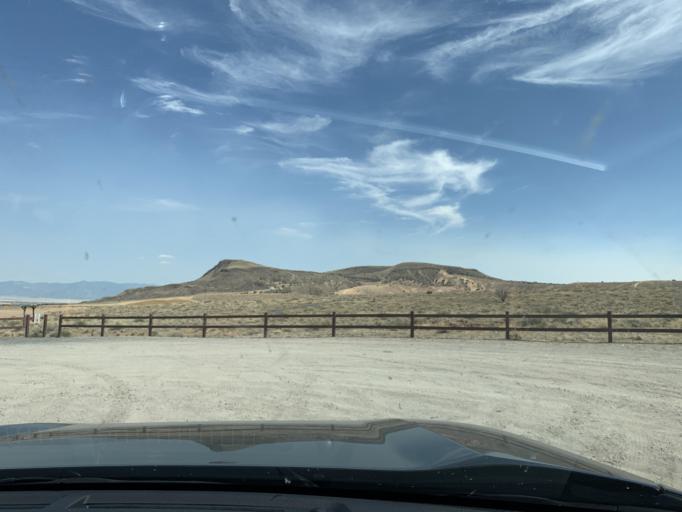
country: US
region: New Mexico
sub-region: Valencia County
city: Los Lunas
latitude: 34.8224
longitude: -106.8117
